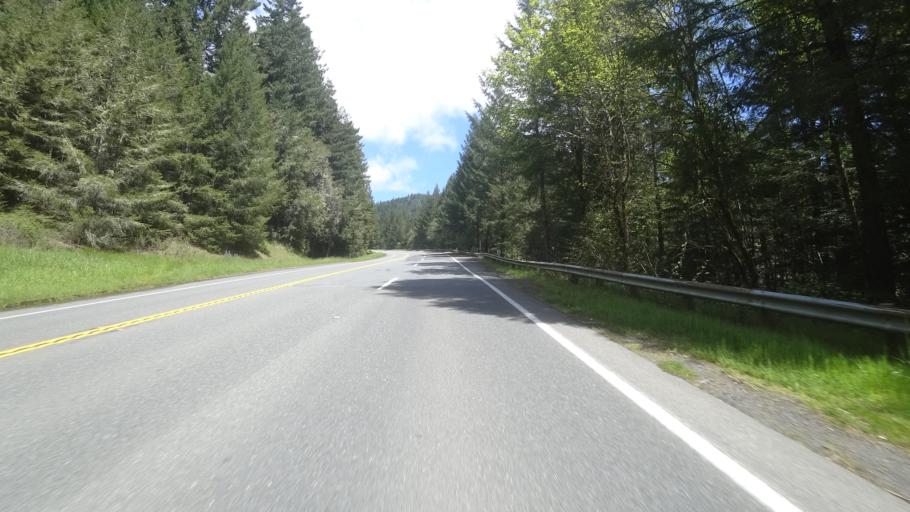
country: US
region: California
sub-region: Humboldt County
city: Blue Lake
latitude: 40.9207
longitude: -123.9109
